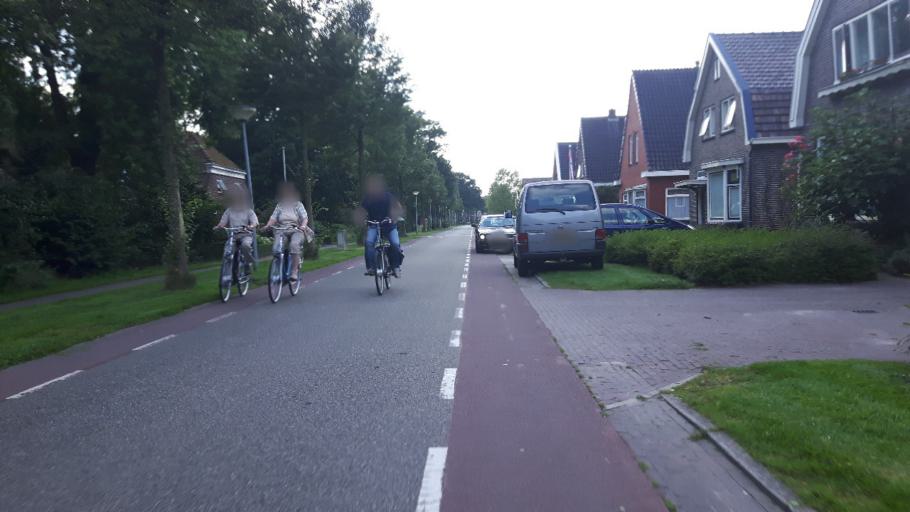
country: NL
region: Drenthe
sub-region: Gemeente Tynaarlo
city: Vries
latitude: 53.0784
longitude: 6.5867
